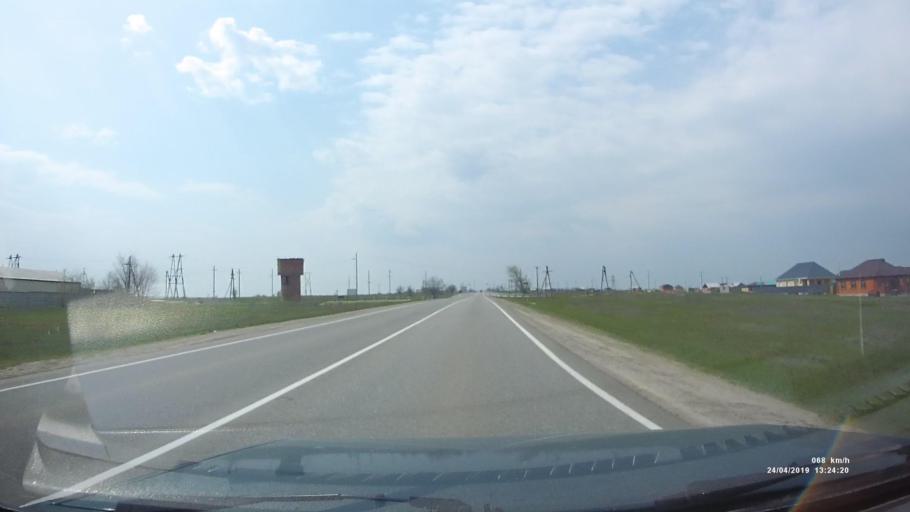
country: RU
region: Kalmykiya
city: Elista
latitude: 46.2839
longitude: 44.2564
